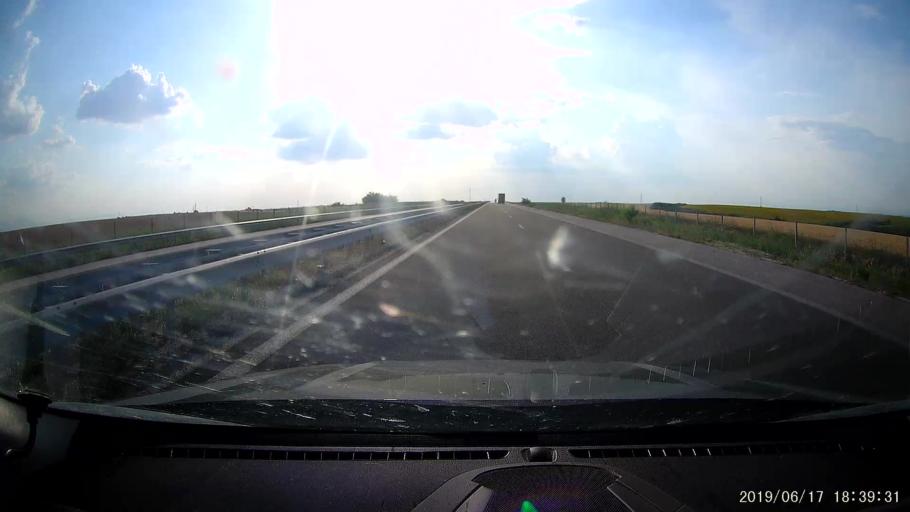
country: BG
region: Stara Zagora
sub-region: Obshtina Chirpan
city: Chirpan
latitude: 42.1458
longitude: 25.3050
